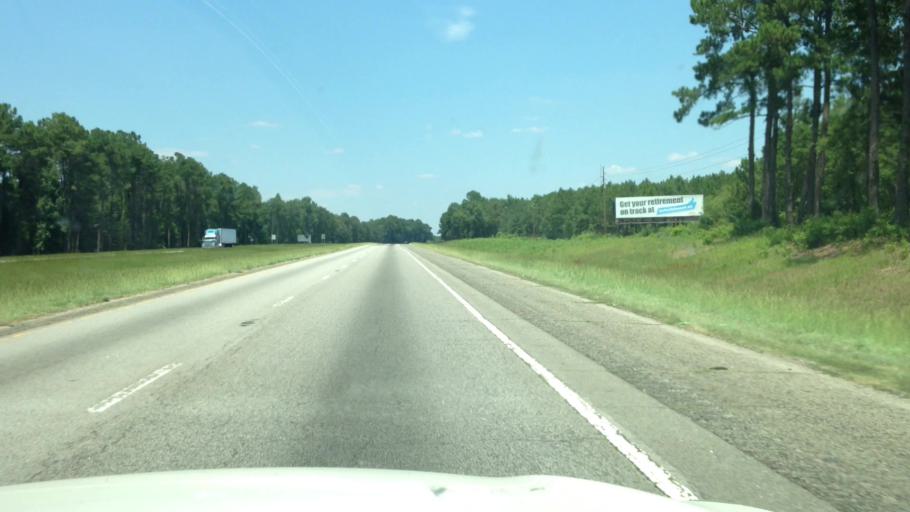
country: US
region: South Carolina
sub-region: Dillon County
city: Dillon
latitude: 34.4703
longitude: -79.3461
